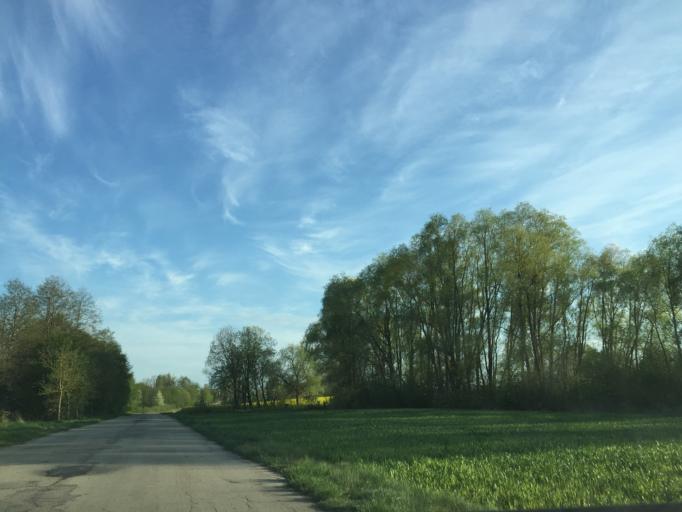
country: LV
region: Bauskas Rajons
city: Bauska
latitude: 56.3184
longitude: 24.2742
